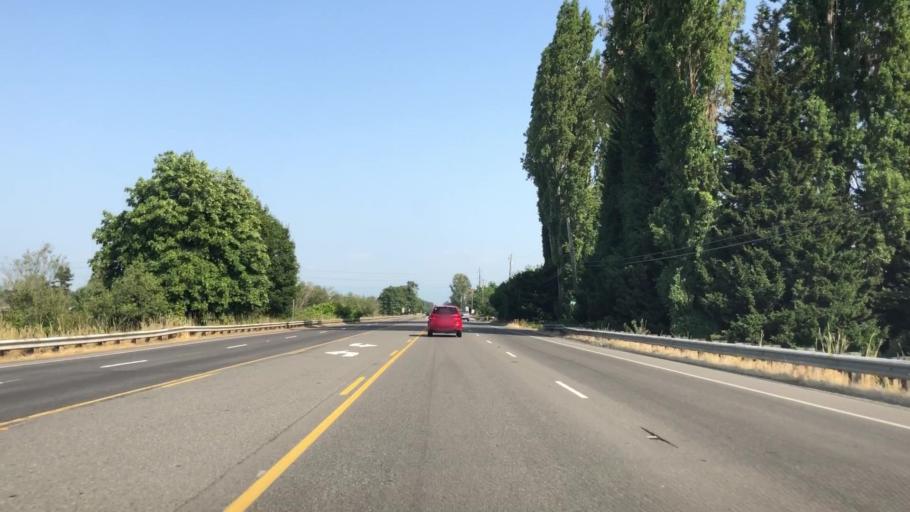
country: US
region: Washington
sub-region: Pierce County
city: Fife
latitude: 47.2292
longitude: -122.3756
